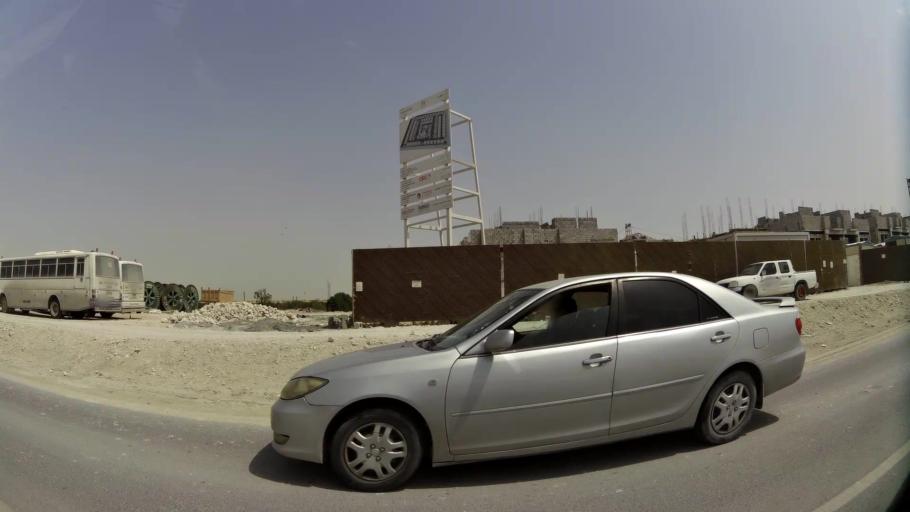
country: QA
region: Baladiyat ar Rayyan
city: Ar Rayyan
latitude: 25.2307
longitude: 51.4087
